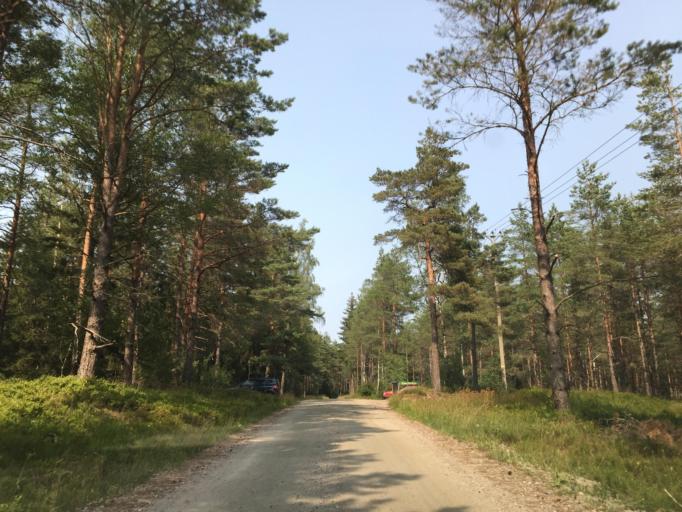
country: SE
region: Vaestra Goetaland
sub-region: Lilla Edets Kommun
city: Lilla Edet
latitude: 58.2488
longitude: 12.0879
